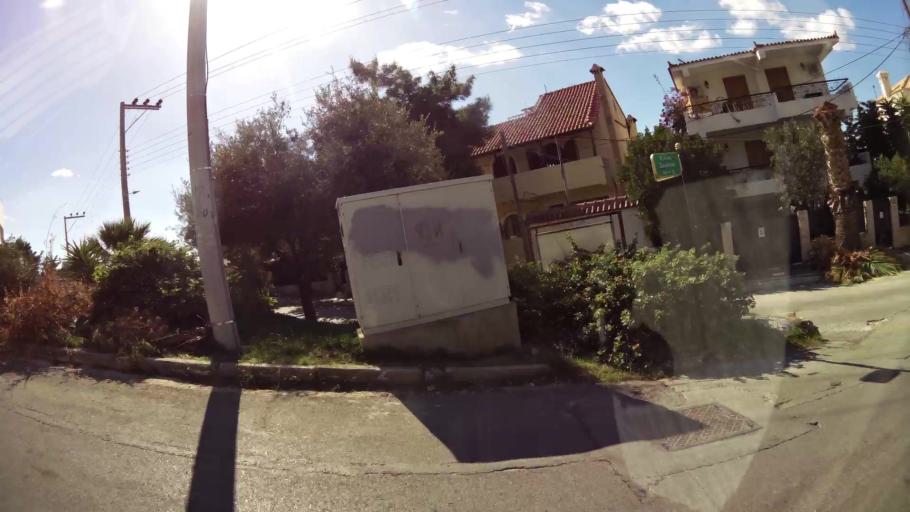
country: GR
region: Attica
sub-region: Nomarchia Anatolikis Attikis
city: Voula
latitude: 37.8486
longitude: 23.7804
